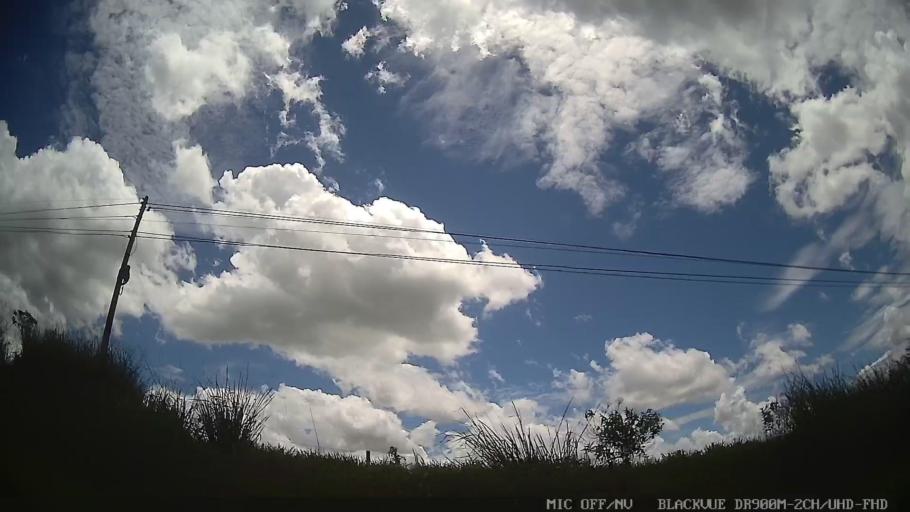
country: BR
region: Sao Paulo
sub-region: Jaguariuna
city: Jaguariuna
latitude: -22.7122
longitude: -46.9566
